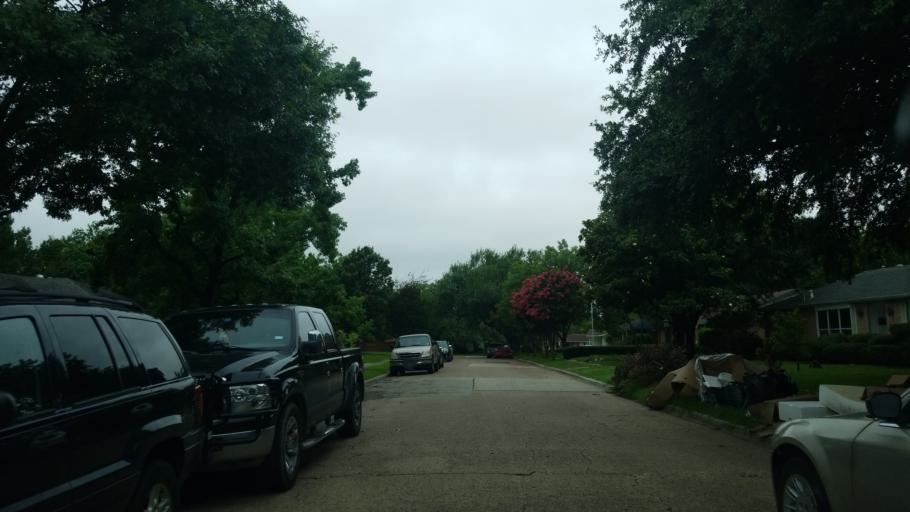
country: US
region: Texas
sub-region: Dallas County
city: Farmers Branch
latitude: 32.8941
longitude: -96.8742
